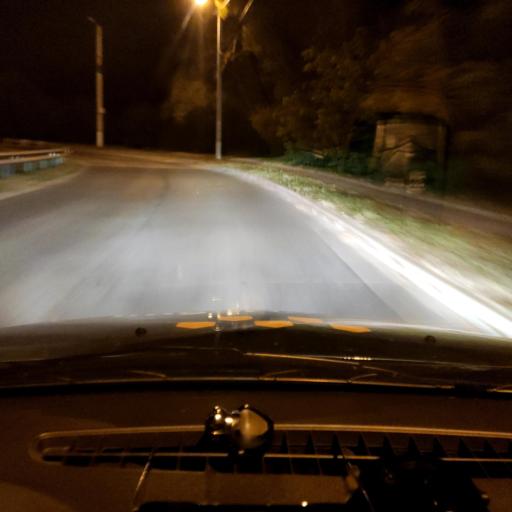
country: RU
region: Belgorod
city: Mayskiy
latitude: 50.5163
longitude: 36.4633
